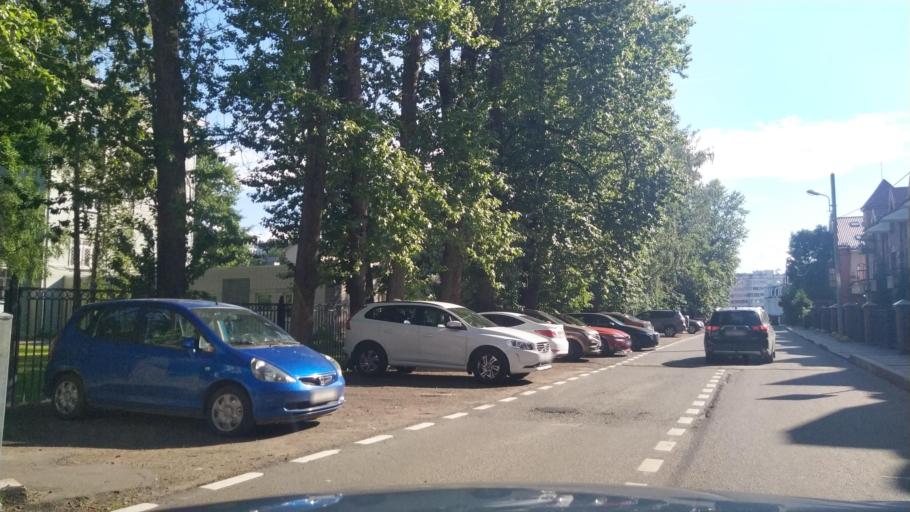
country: RU
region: St.-Petersburg
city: Kolomyagi
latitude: 60.0172
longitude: 30.2955
